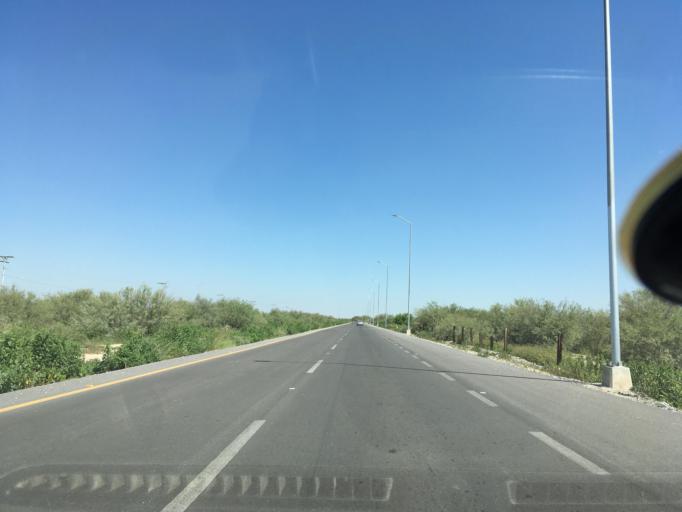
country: MX
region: Coahuila
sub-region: Torreon
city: Fraccionamiento la Noria
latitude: 25.4820
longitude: -103.3194
